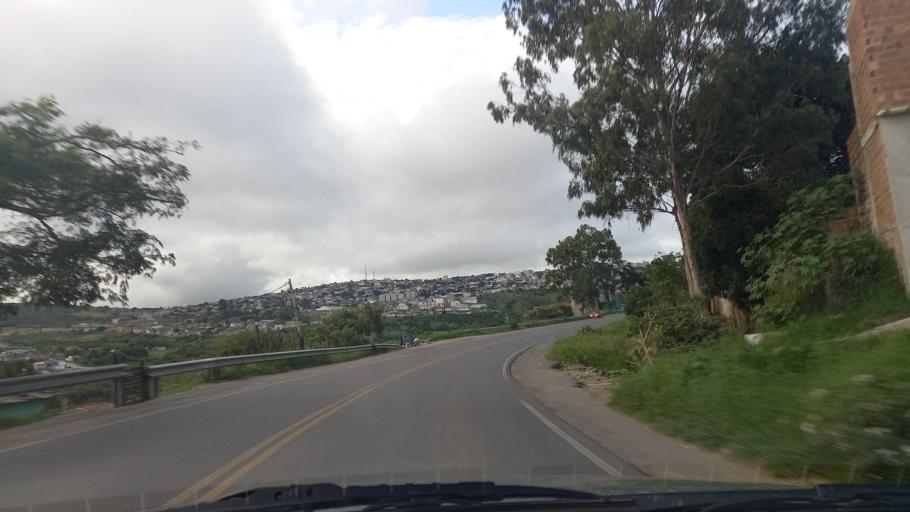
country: BR
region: Pernambuco
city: Garanhuns
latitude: -8.8986
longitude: -36.5030
